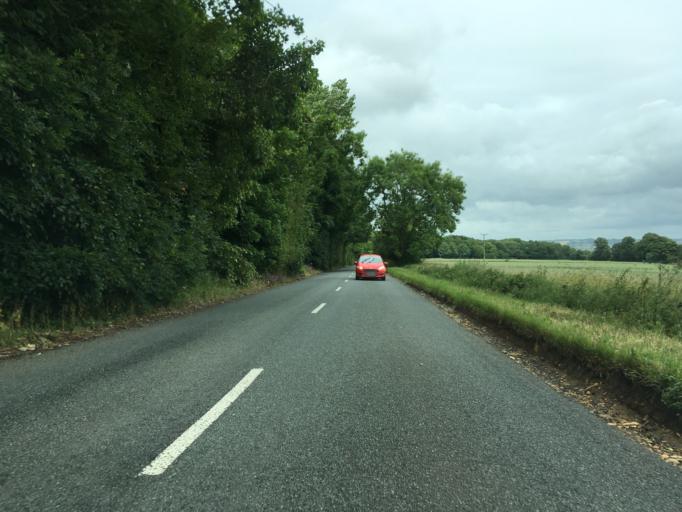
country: GB
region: England
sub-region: Worcestershire
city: Broadway
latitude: 52.0437
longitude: -1.8154
